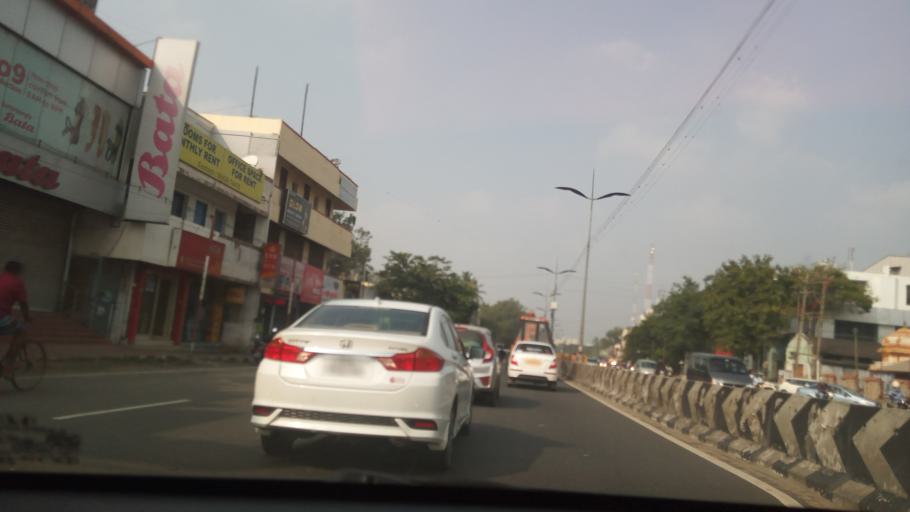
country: IN
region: Tamil Nadu
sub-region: Coimbatore
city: Singanallur
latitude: 11.0256
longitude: 77.0165
